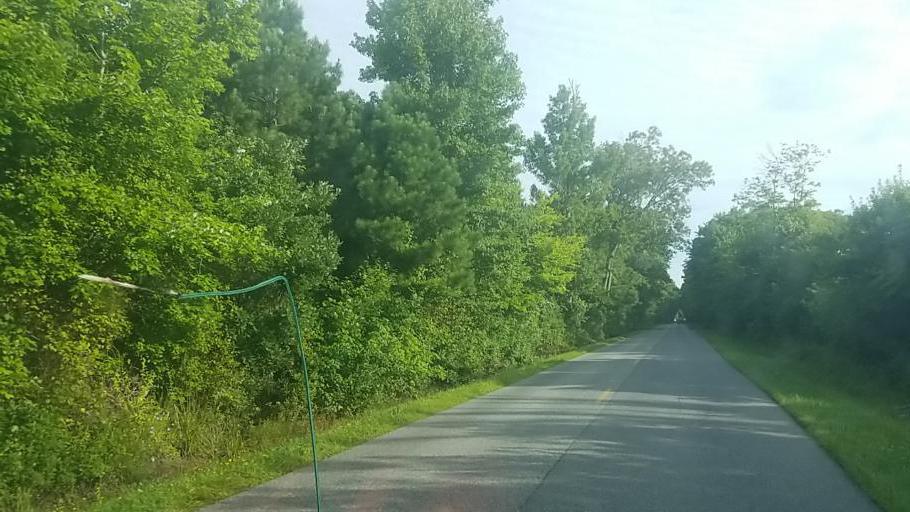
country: US
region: Maryland
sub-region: Worcester County
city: West Ocean City
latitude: 38.3330
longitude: -75.1559
